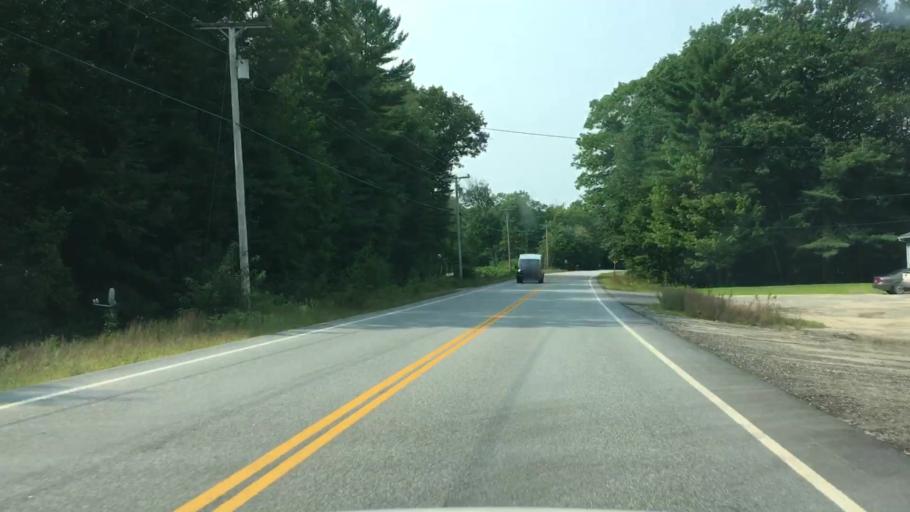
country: US
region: Maine
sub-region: Androscoggin County
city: Livermore
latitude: 44.3323
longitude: -70.2889
